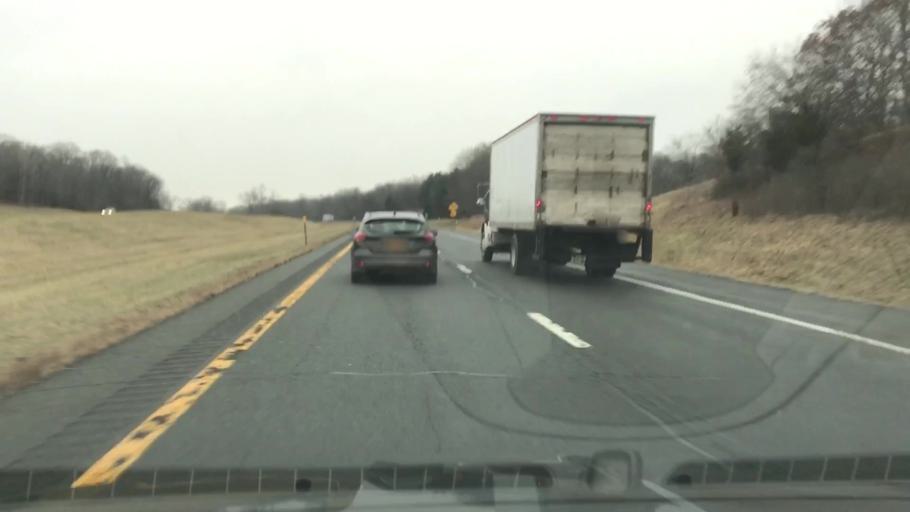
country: US
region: New York
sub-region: Orange County
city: Otisville
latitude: 41.3972
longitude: -74.5389
